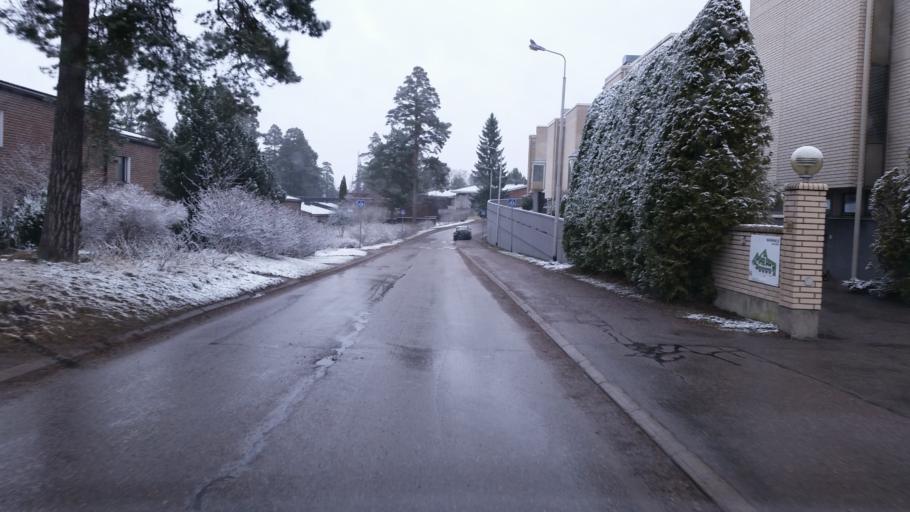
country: FI
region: Uusimaa
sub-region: Helsinki
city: Koukkuniemi
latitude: 60.1660
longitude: 24.7932
